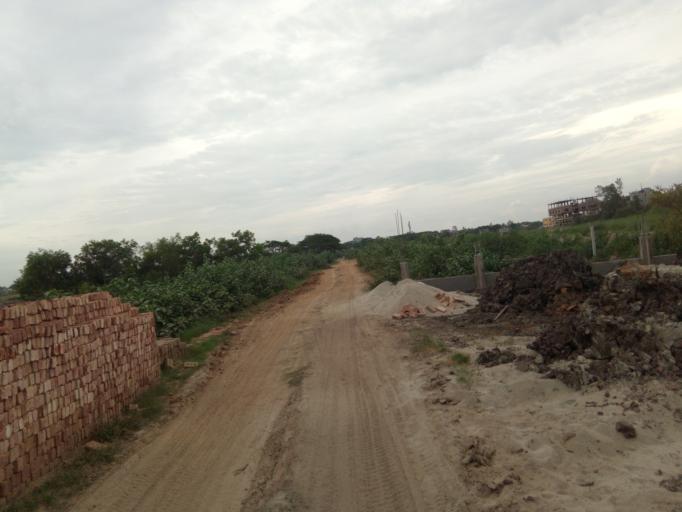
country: BD
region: Dhaka
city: Paltan
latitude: 23.7390
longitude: 90.4730
